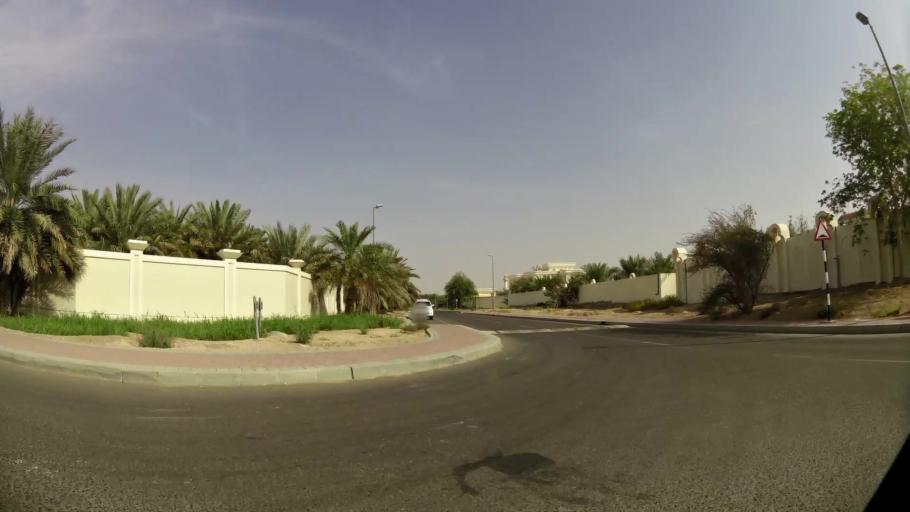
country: AE
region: Abu Dhabi
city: Al Ain
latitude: 24.1462
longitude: 55.7028
